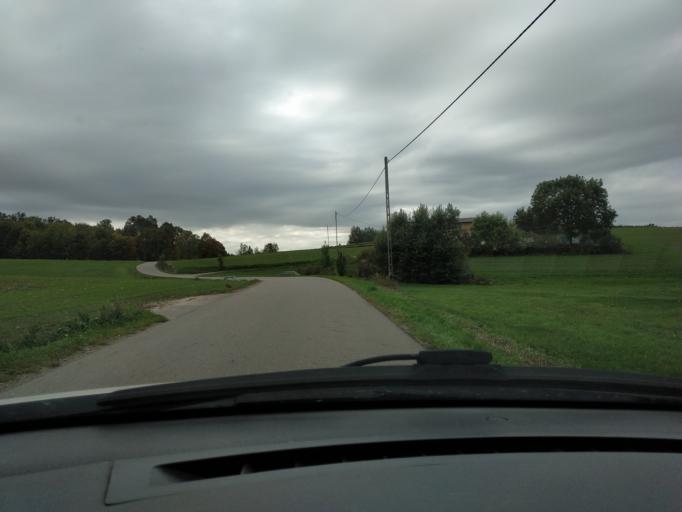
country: PL
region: Warmian-Masurian Voivodeship
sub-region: Powiat nowomiejski
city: Biskupiec
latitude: 53.4567
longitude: 19.3158
